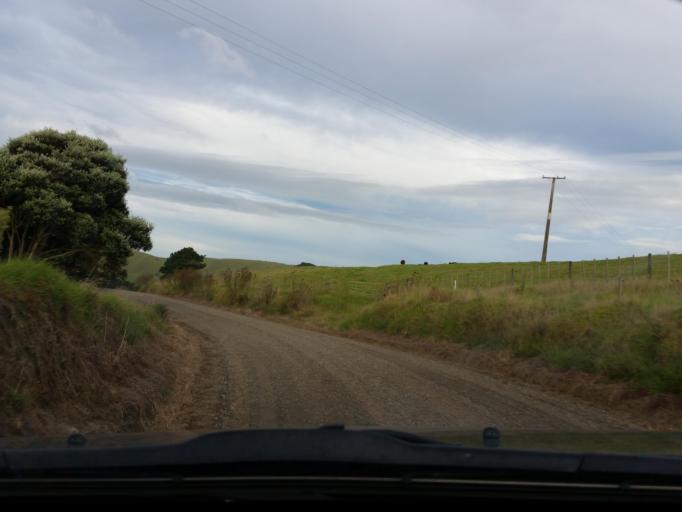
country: NZ
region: Northland
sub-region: Kaipara District
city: Dargaville
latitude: -35.8794
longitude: 173.6940
